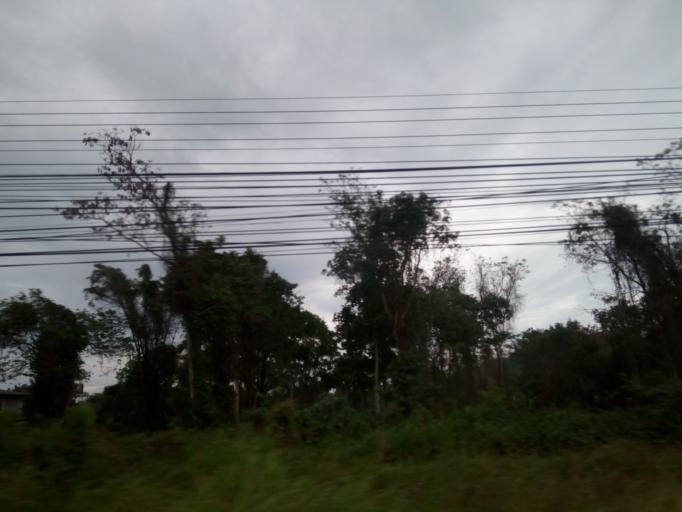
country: TH
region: Phuket
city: Thalang
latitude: 8.0664
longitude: 98.3961
